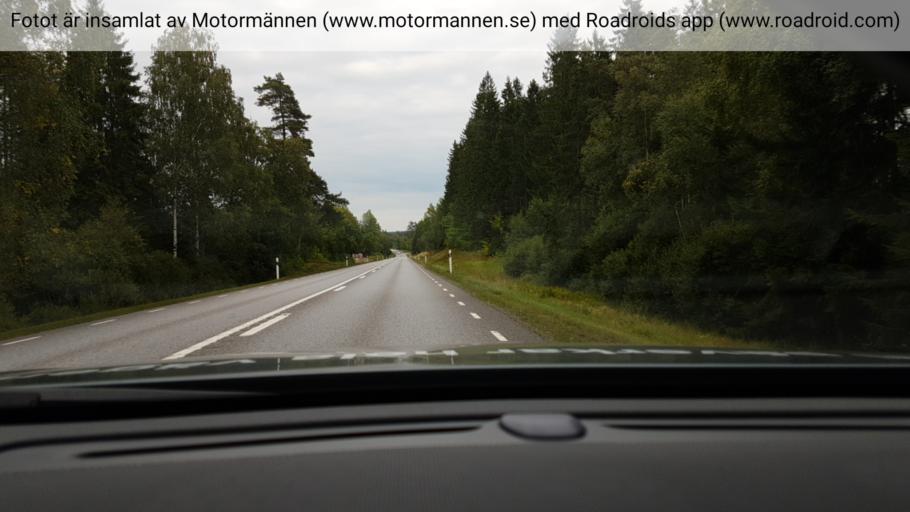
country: SE
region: Joenkoeping
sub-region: Gislaveds Kommun
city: Reftele
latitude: 57.1568
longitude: 13.5192
